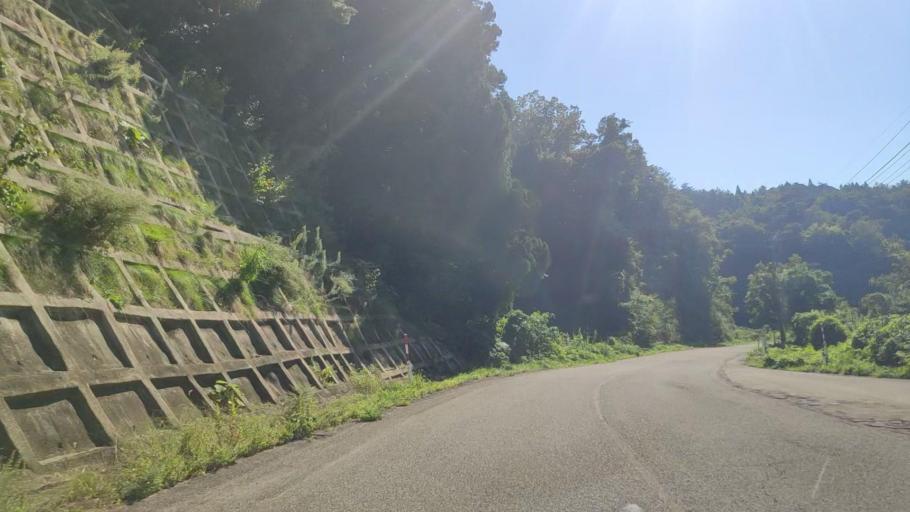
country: JP
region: Ishikawa
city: Nanao
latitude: 37.3161
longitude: 137.1646
